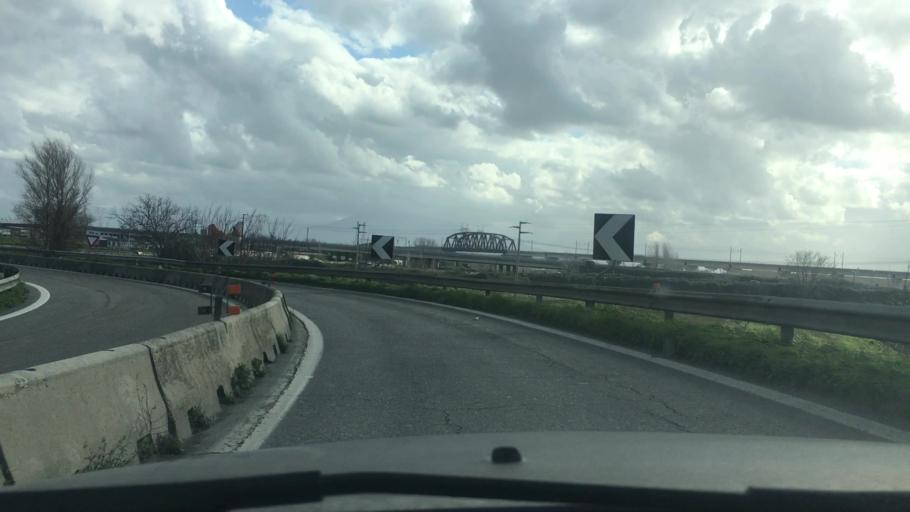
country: IT
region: Campania
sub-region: Provincia di Caserta
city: Marcianise
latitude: 41.0188
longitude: 14.3203
